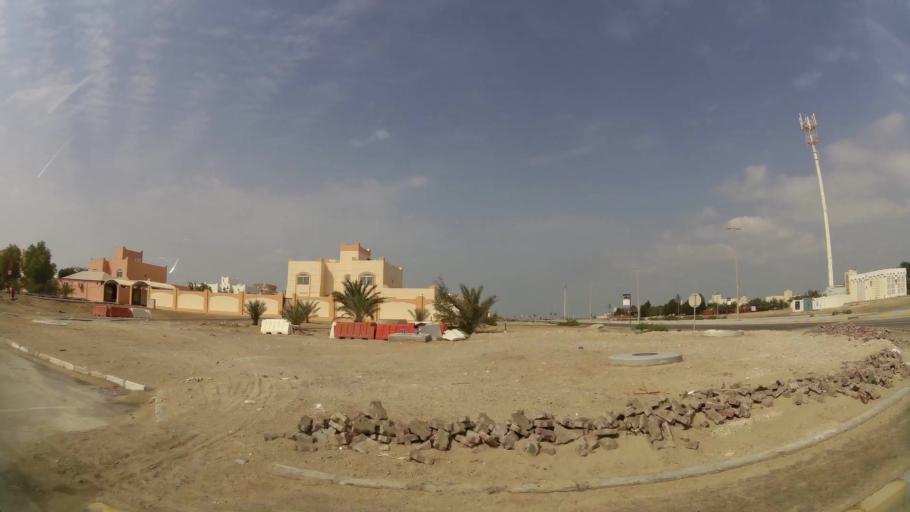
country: AE
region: Abu Dhabi
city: Abu Dhabi
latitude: 24.5586
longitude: 54.6418
